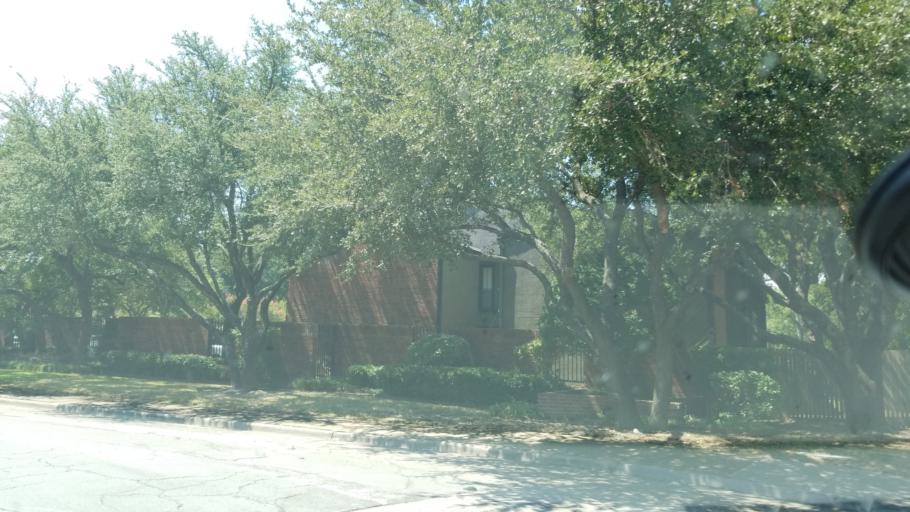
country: US
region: Texas
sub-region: Dallas County
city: Richardson
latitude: 32.9053
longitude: -96.7200
